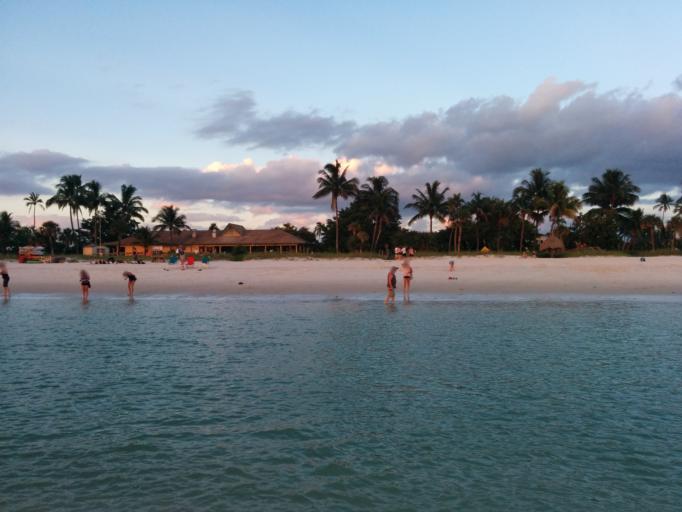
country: US
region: Florida
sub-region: Collier County
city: Naples
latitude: 26.1625
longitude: -81.8115
